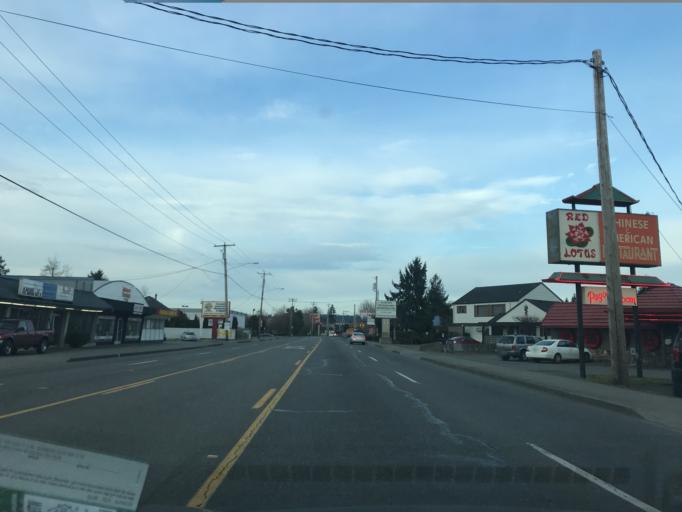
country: US
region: Washington
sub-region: King County
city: Auburn
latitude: 47.3133
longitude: -122.2252
